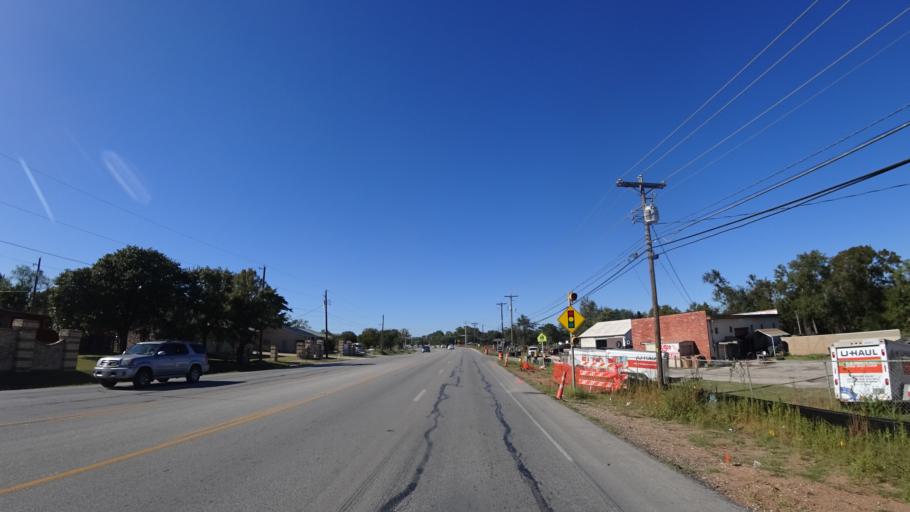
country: US
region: Texas
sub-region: Travis County
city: Hornsby Bend
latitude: 30.2754
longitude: -97.6359
